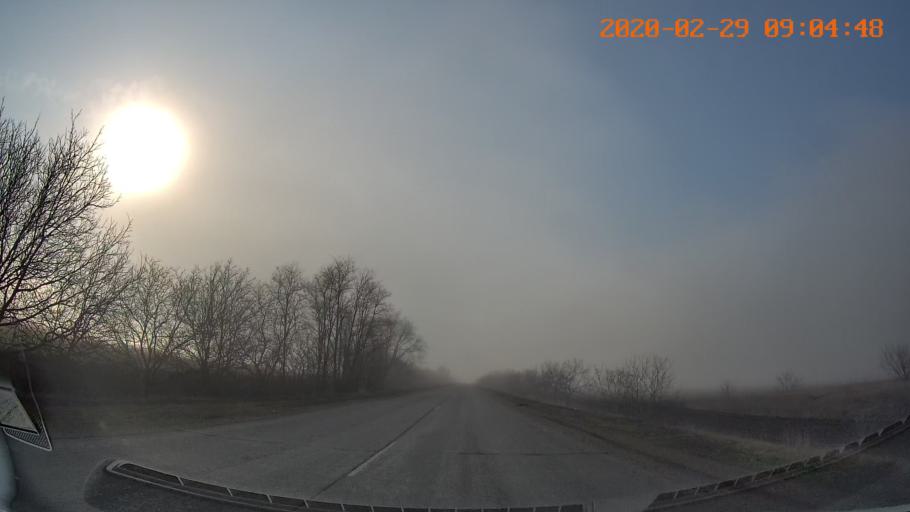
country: MD
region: Telenesti
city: Tiraspolul Nou
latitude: 46.8975
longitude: 29.7376
